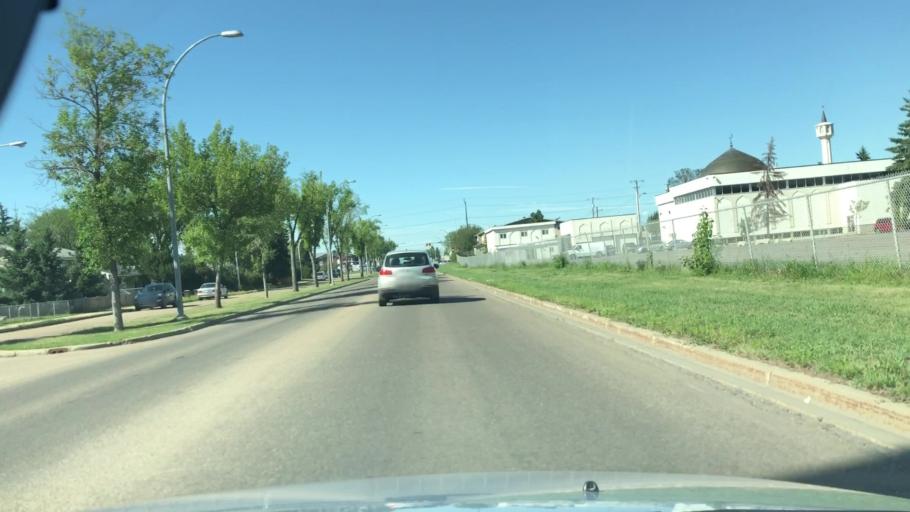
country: CA
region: Alberta
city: Edmonton
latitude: 53.5900
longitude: -113.5165
